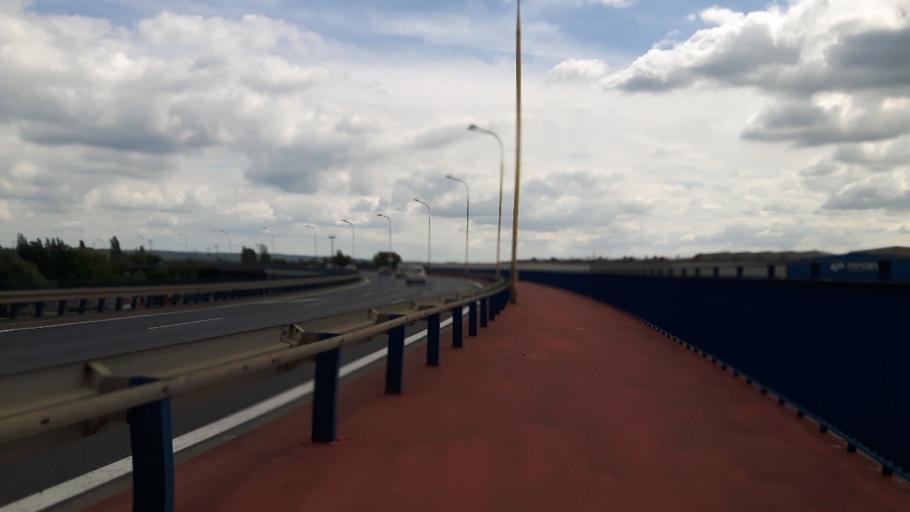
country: PL
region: West Pomeranian Voivodeship
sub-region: Szczecin
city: Szczecin
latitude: 53.4176
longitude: 14.5653
